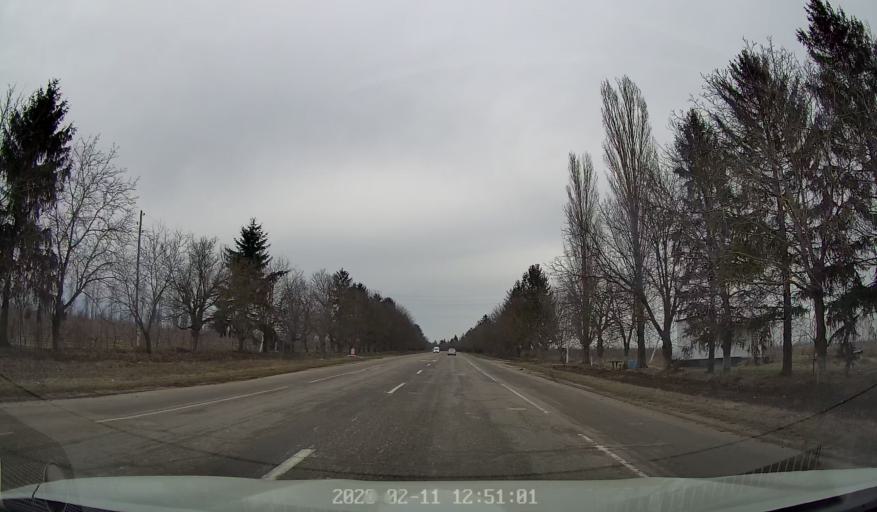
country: MD
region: Briceni
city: Briceni
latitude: 48.3030
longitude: 27.1243
